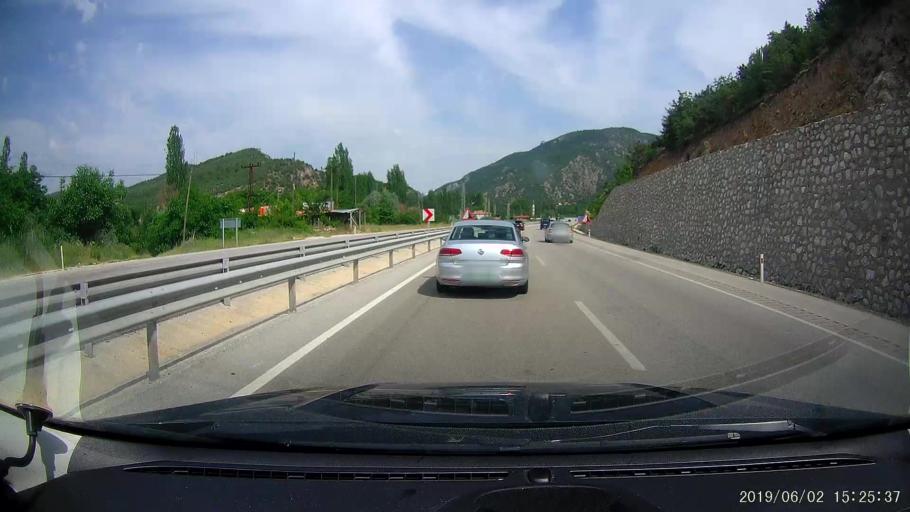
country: TR
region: Amasya
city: Saraycik
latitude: 40.9938
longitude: 35.0240
